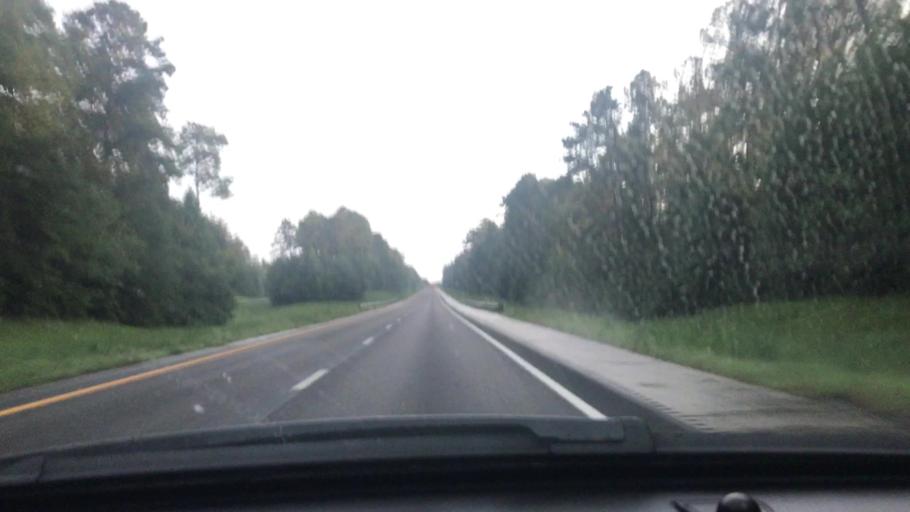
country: US
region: Mississippi
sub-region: Pike County
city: Magnolia
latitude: 31.0796
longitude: -90.4909
